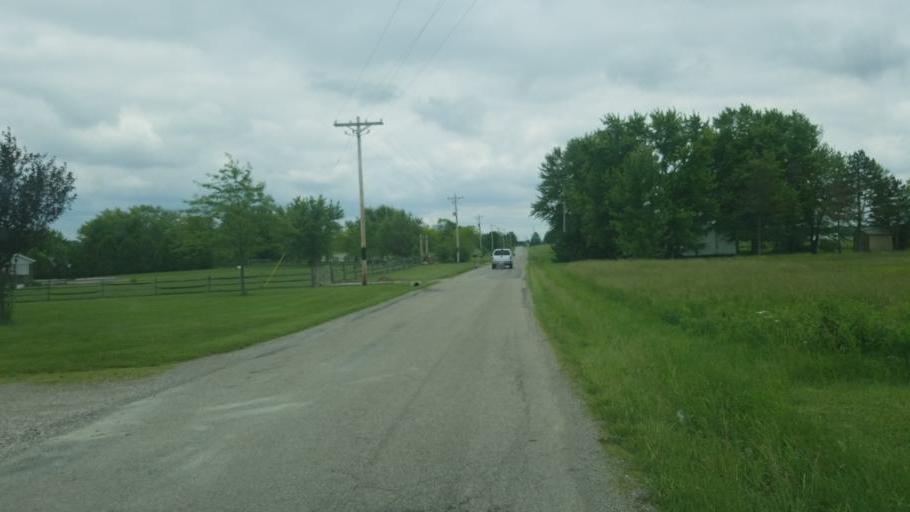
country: US
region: Ohio
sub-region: Fairfield County
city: Millersport
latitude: 39.8812
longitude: -82.5063
